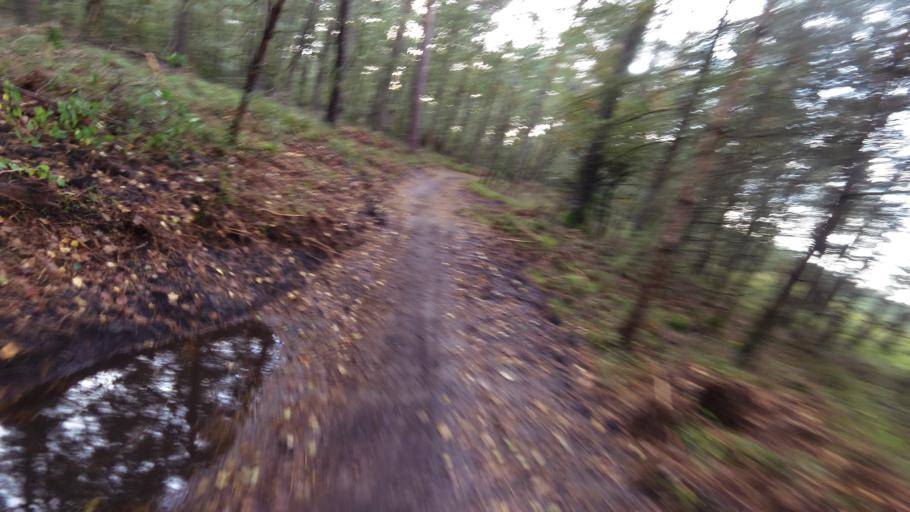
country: NL
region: Gelderland
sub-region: Gemeente Renkum
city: Wolfheze
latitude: 52.0363
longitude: 5.7880
